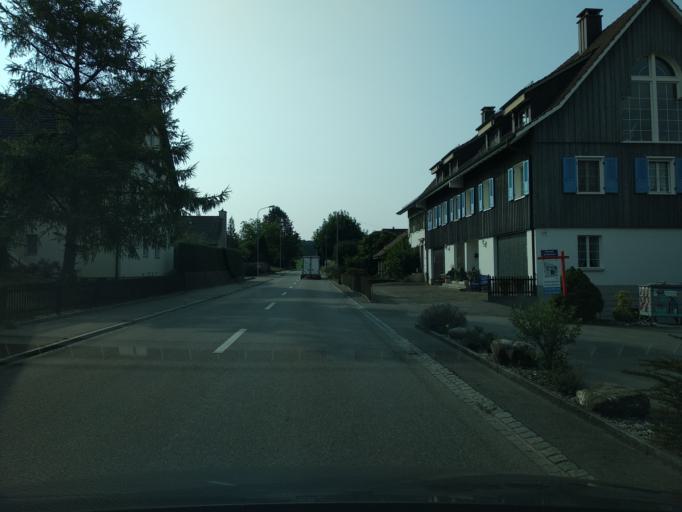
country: DE
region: Baden-Wuerttemberg
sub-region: Freiburg Region
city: Busingen
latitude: 47.6597
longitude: 8.7043
